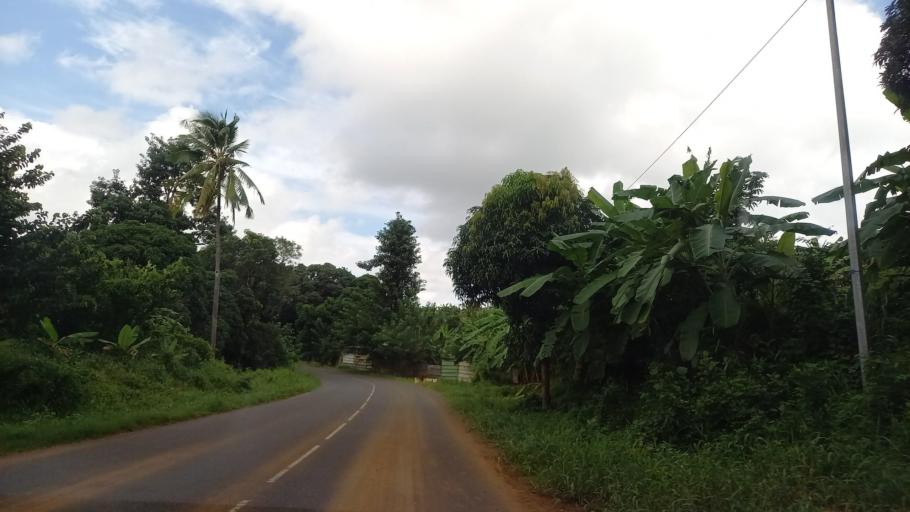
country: YT
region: Boueni
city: Boueni
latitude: -12.9202
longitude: 45.1018
